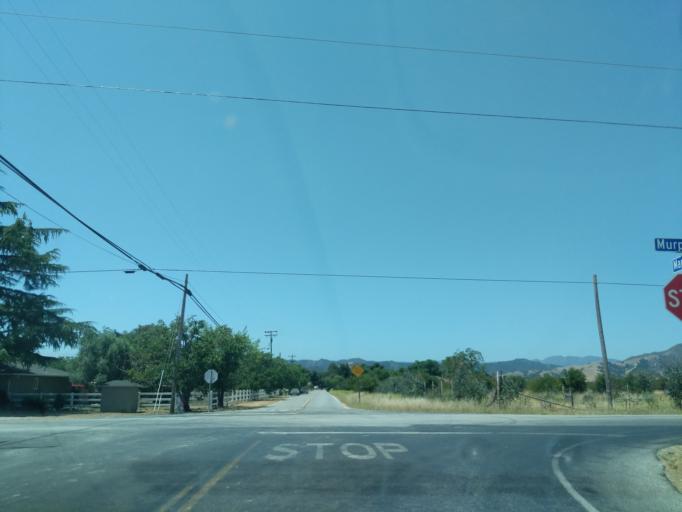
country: US
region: California
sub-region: Santa Clara County
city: San Martin
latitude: 37.1128
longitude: -121.6159
